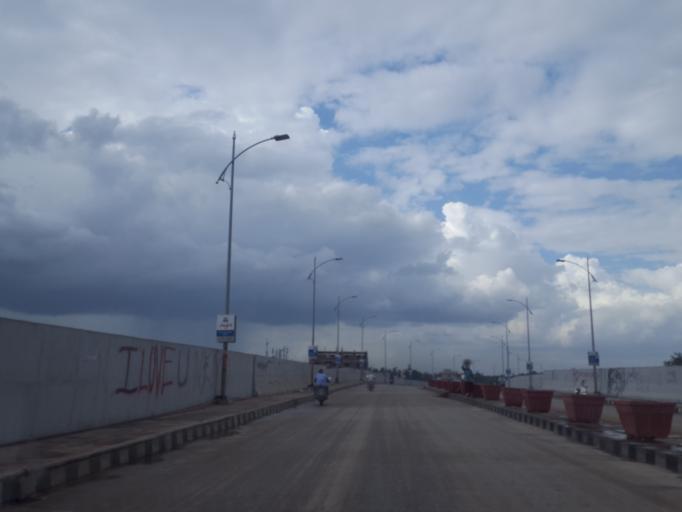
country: IN
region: Telangana
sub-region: Medak
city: Serilingampalle
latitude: 17.4809
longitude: 78.3110
